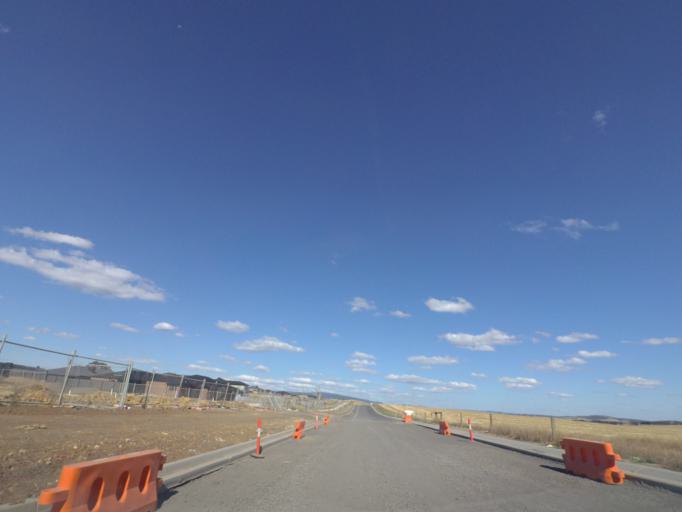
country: AU
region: Victoria
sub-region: Hume
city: Craigieburn
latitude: -37.4208
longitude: 144.9586
